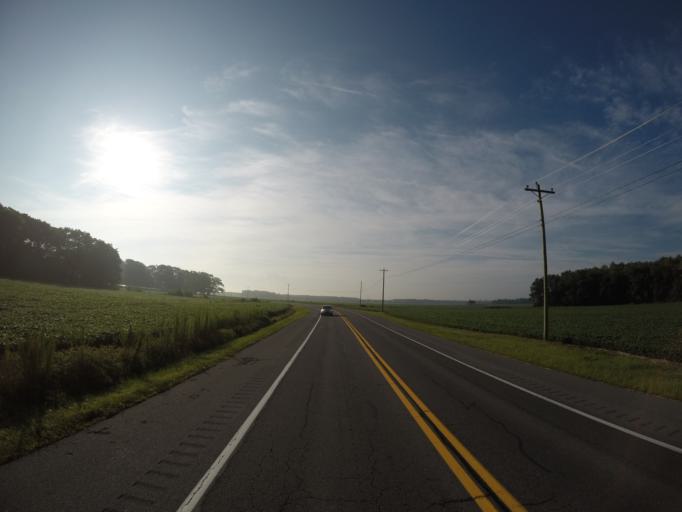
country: US
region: Delaware
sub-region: Sussex County
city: Selbyville
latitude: 38.5244
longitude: -75.1955
